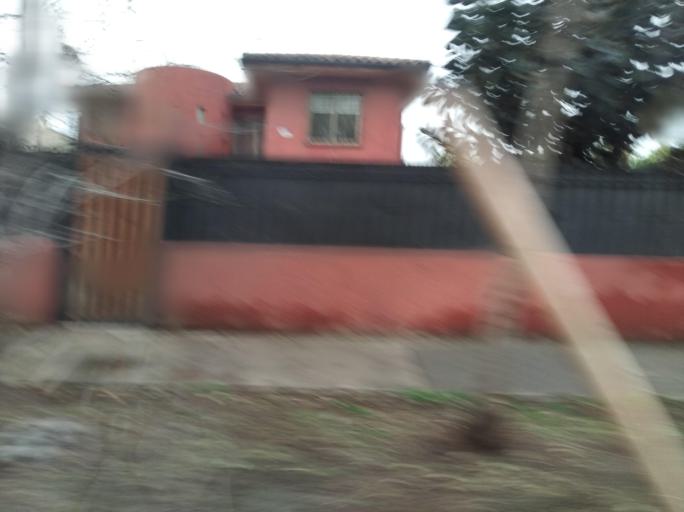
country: CL
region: Santiago Metropolitan
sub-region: Provincia de Santiago
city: Villa Presidente Frei, Nunoa, Santiago, Chile
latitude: -33.4884
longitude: -70.5979
